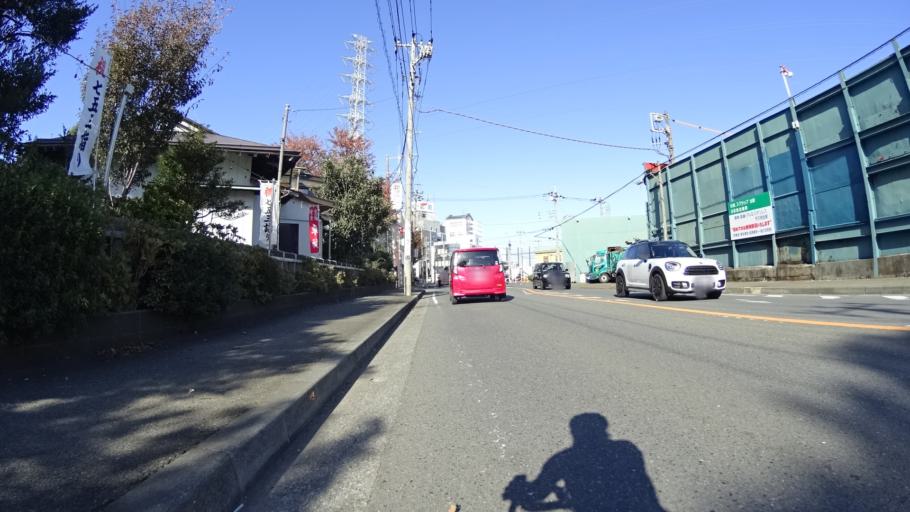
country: JP
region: Tokyo
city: Hachioji
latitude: 35.5815
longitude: 139.3616
